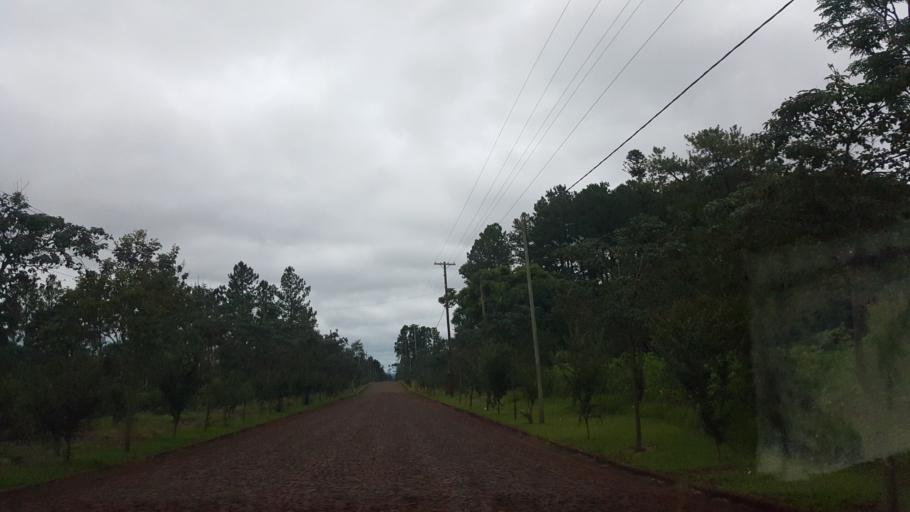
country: AR
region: Misiones
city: Capiovi
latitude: -26.9560
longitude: -55.0559
